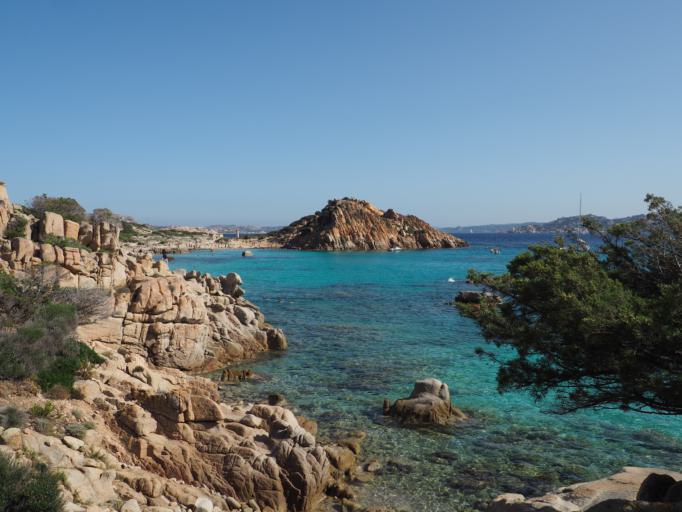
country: IT
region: Sardinia
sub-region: Provincia di Olbia-Tempio
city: Palau
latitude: 41.2311
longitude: 9.3428
